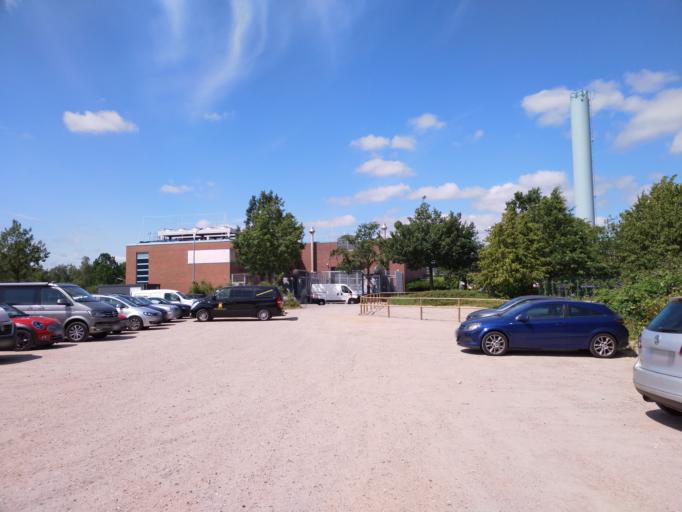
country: DE
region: Schleswig-Holstein
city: Norderstedt
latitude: 53.7043
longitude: 9.9937
